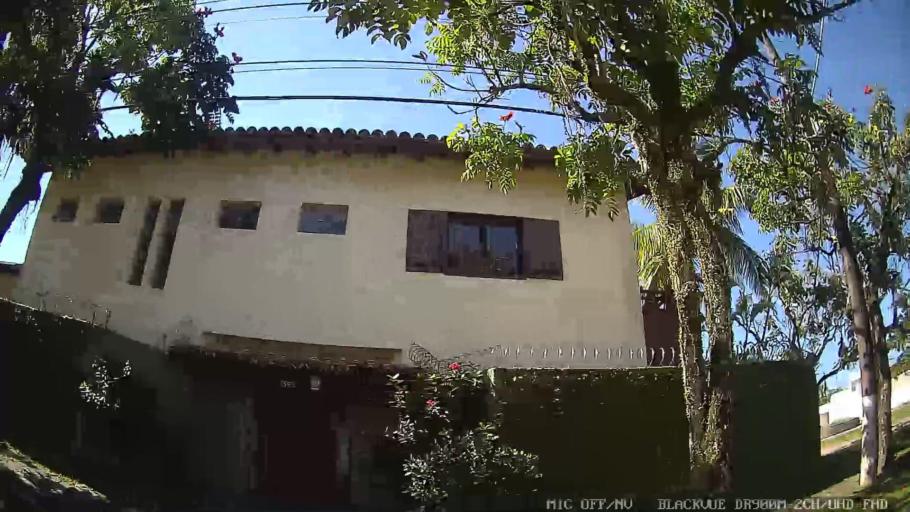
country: BR
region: Sao Paulo
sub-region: Guaruja
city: Guaruja
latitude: -23.9817
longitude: -46.2115
